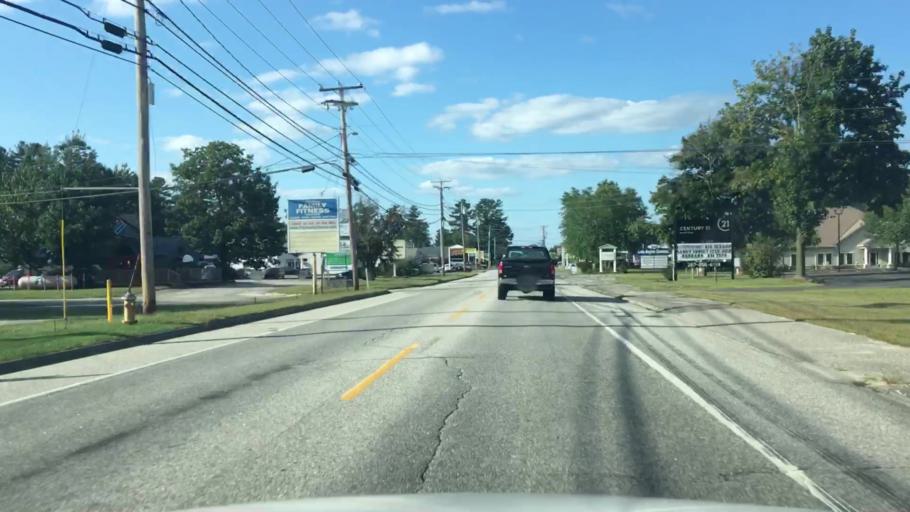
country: US
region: Maine
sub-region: Cumberland County
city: North Windham
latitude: 43.8231
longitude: -70.4342
